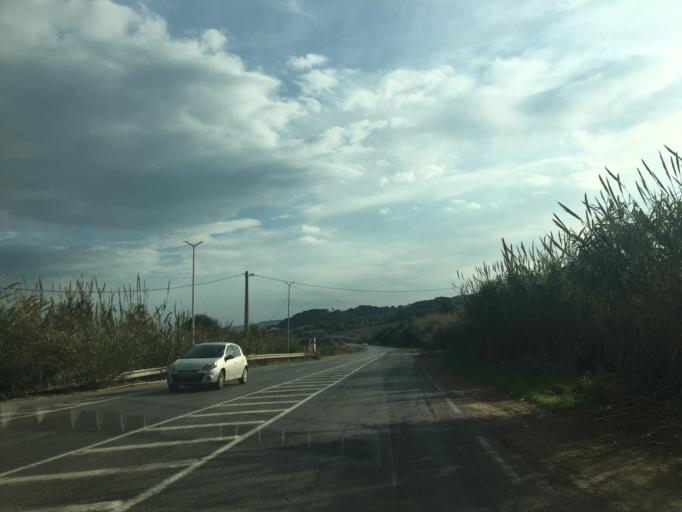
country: DZ
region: Tipaza
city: Tipasa
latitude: 36.5899
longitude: 2.4895
